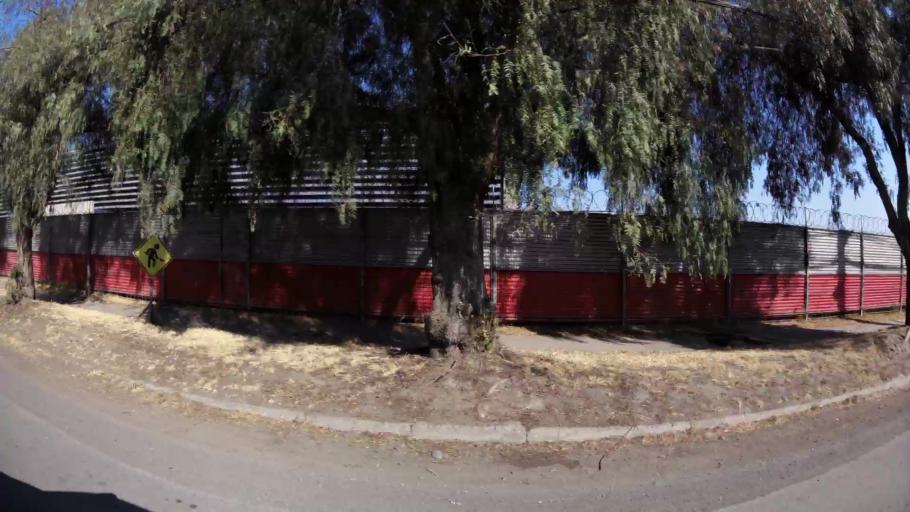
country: CL
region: Santiago Metropolitan
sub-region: Provincia de Chacabuco
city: Chicureo Abajo
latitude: -33.3315
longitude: -70.7190
